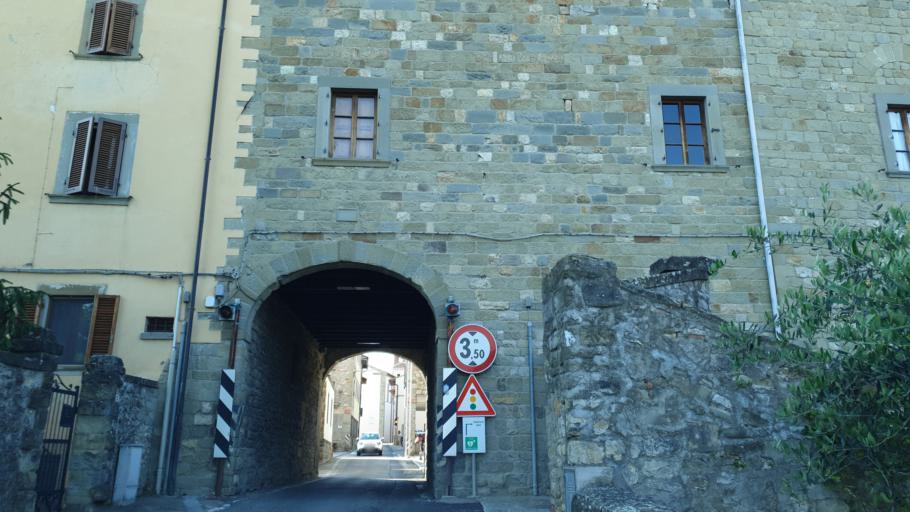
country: IT
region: Tuscany
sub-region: Province of Arezzo
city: Strada
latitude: 43.7493
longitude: 11.7255
